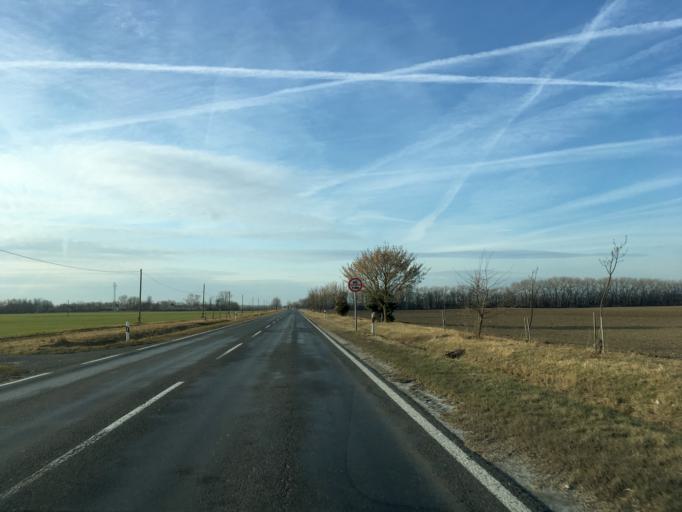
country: HU
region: Gyor-Moson-Sopron
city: Otteveny
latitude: 47.7351
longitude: 17.4762
